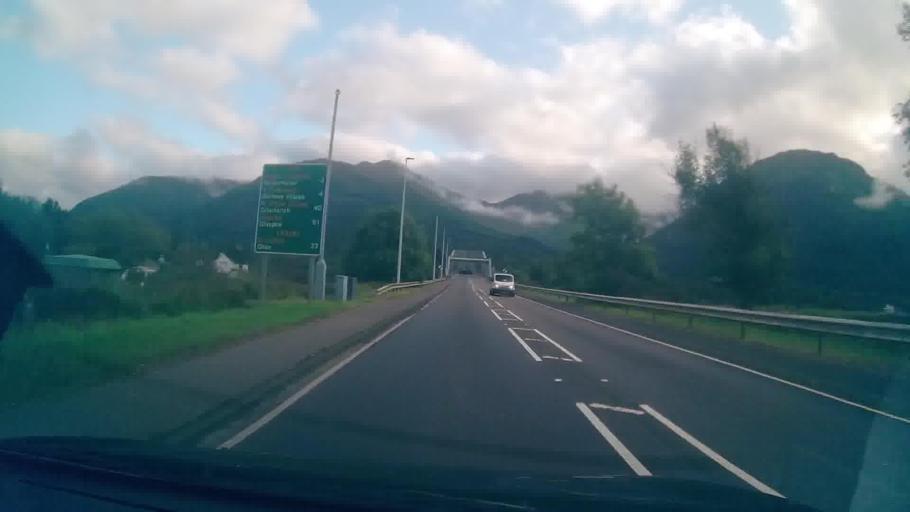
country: GB
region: Scotland
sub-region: Highland
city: Fort William
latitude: 56.6918
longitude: -5.1830
